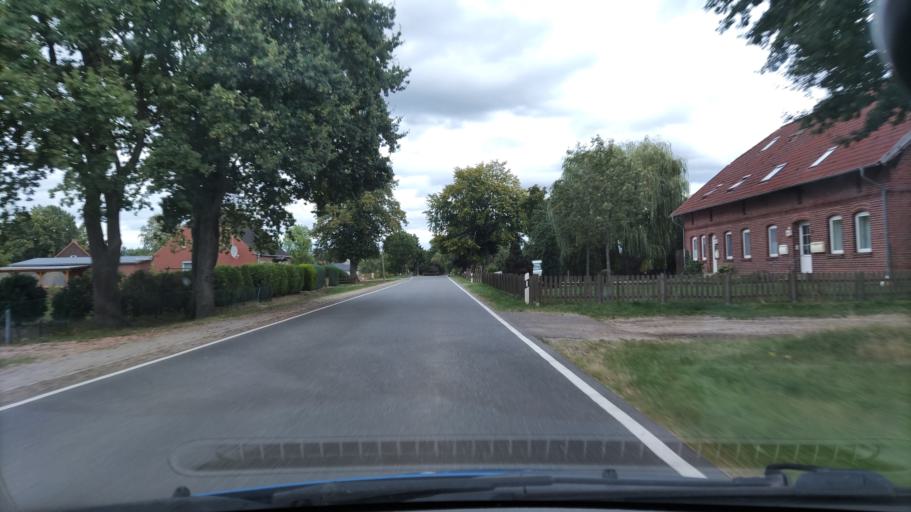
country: DE
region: Lower Saxony
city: Neu Darchau
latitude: 53.2961
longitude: 10.9611
